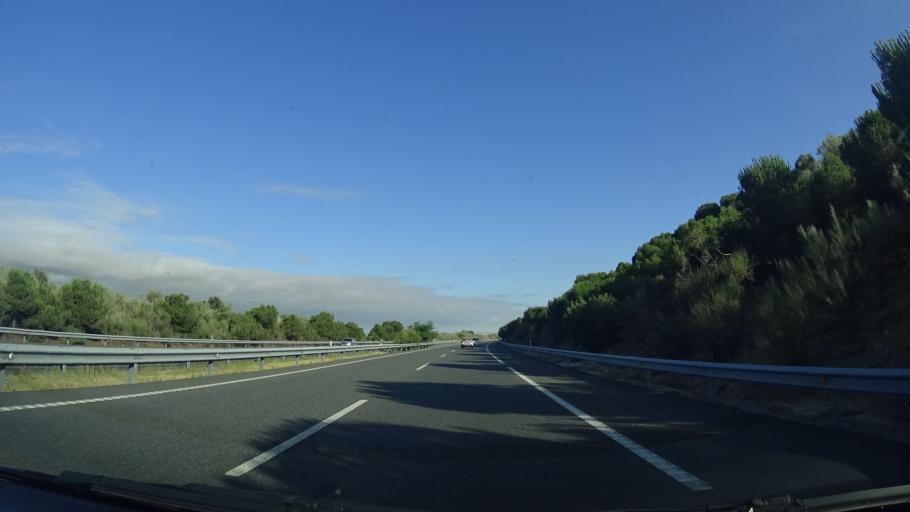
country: ES
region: Castille and Leon
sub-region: Provincia de Segovia
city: Labajos
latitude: 40.8401
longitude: -4.5355
